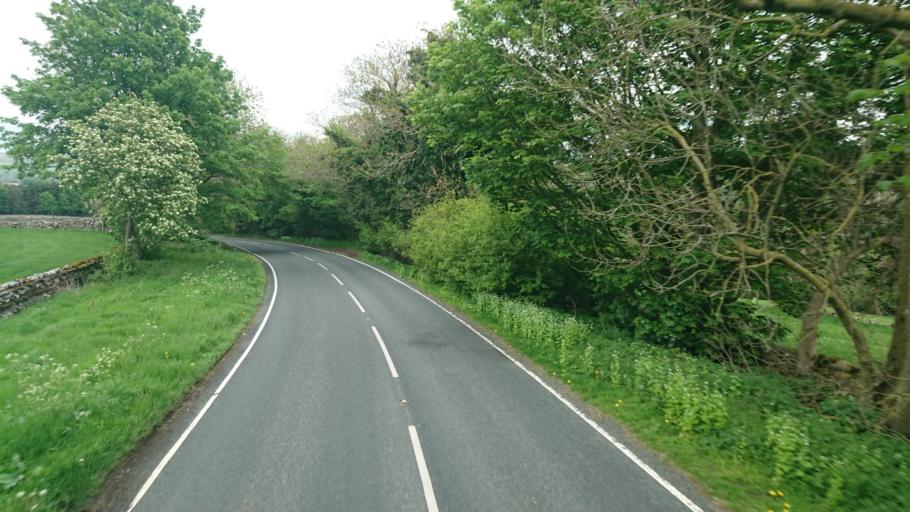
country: GB
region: England
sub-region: North Yorkshire
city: Leyburn
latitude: 54.2903
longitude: -1.9774
